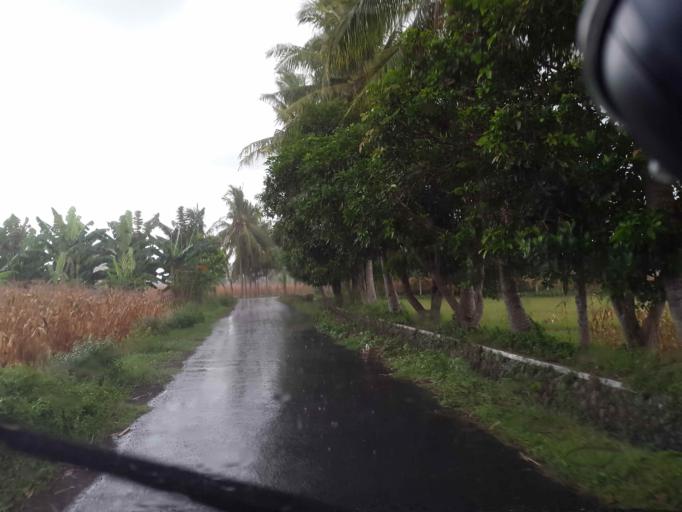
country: ID
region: West Nusa Tenggara
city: Karangkebon Timur
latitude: -8.6721
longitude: 116.1047
